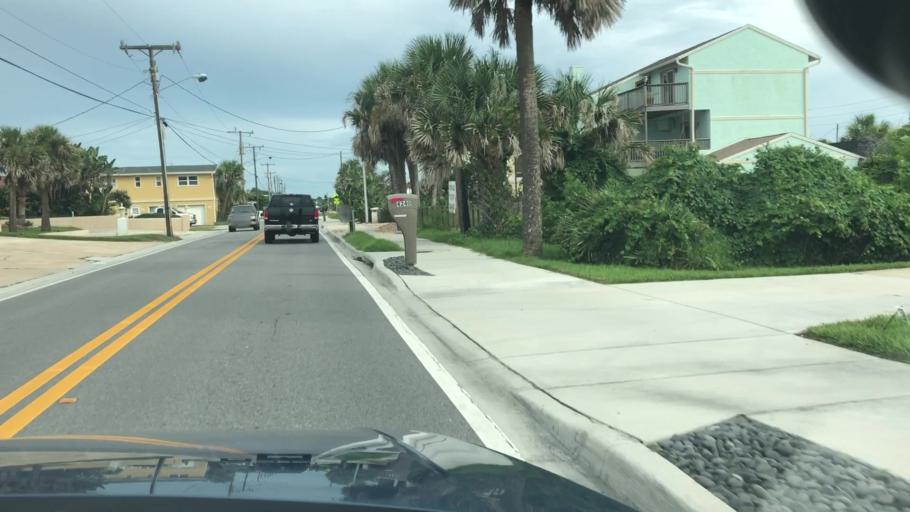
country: US
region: Florida
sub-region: Volusia County
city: Ponce Inlet
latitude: 29.1256
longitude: -80.9545
